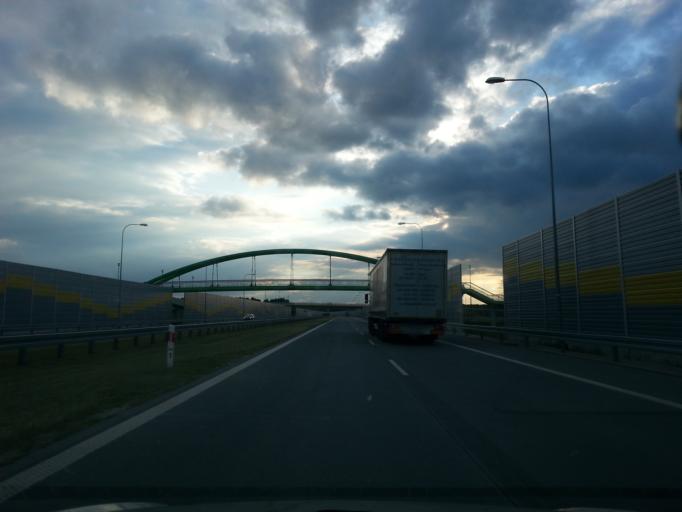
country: PL
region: Lodz Voivodeship
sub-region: Powiat zdunskowolski
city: Zdunska Wola
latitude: 51.5755
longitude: 18.9384
